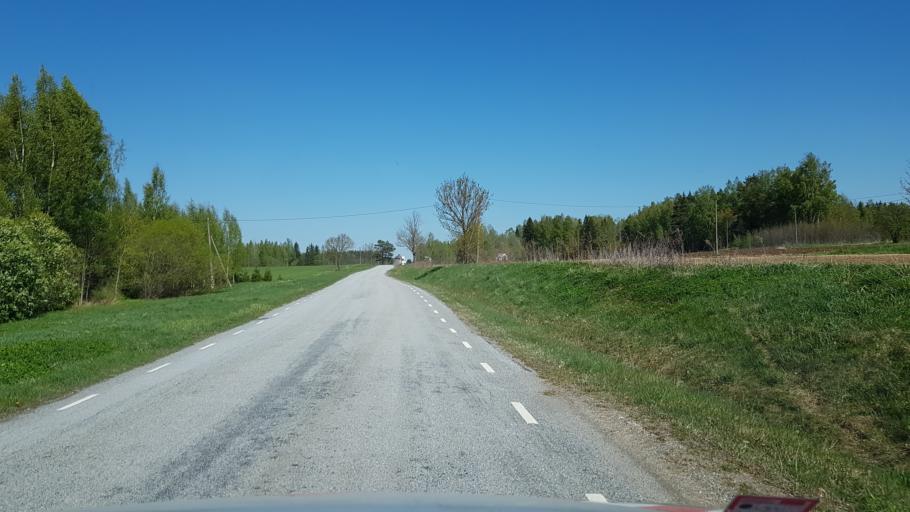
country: EE
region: Vorumaa
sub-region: Voru linn
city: Voru
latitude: 57.9268
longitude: 26.9512
